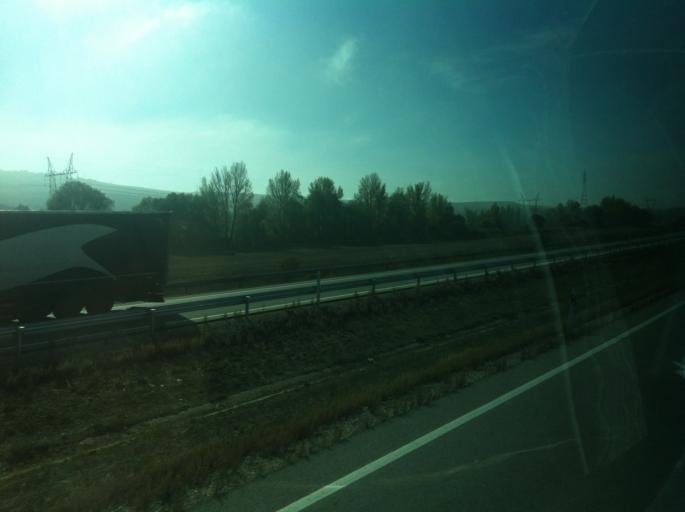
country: ES
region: Castille and Leon
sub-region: Provincia de Burgos
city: Rubena
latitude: 42.4014
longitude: -3.5609
